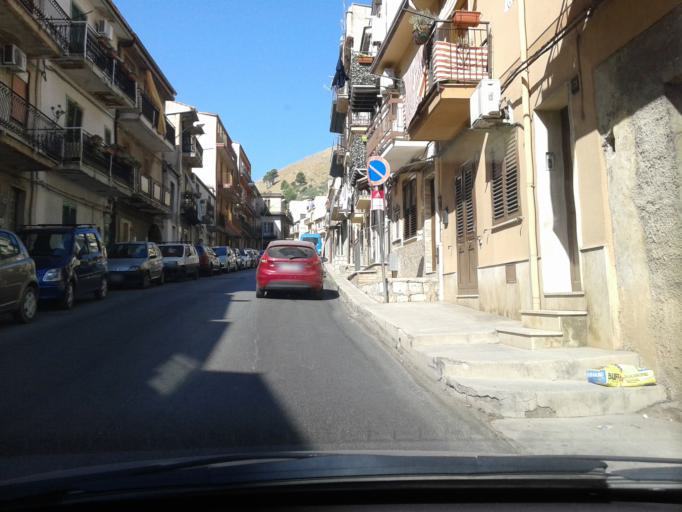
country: IT
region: Sicily
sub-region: Palermo
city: Pioppo
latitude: 38.0488
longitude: 13.2328
